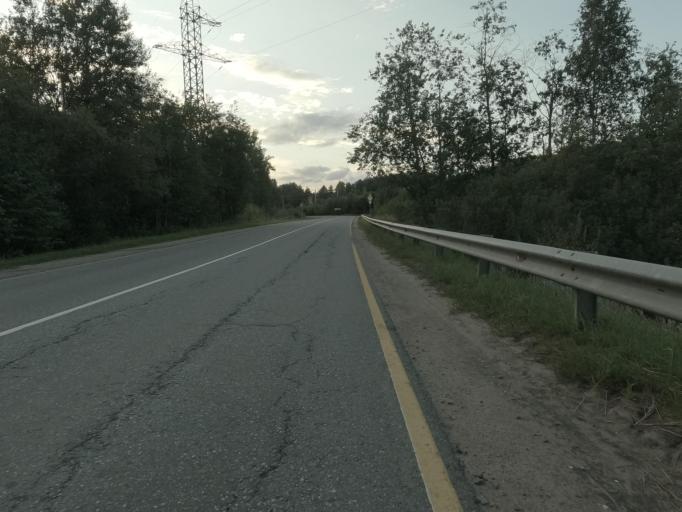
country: RU
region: Leningrad
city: Mga
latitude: 59.7590
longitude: 31.0174
